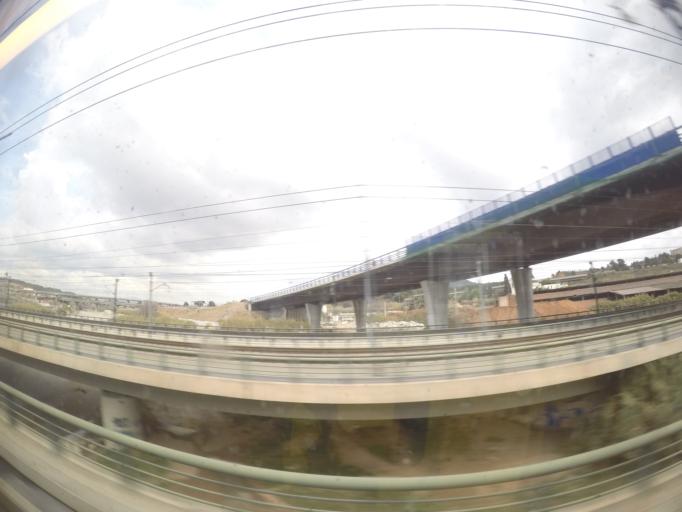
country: ES
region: Catalonia
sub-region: Provincia de Barcelona
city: Palleja
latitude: 41.4412
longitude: 1.9964
